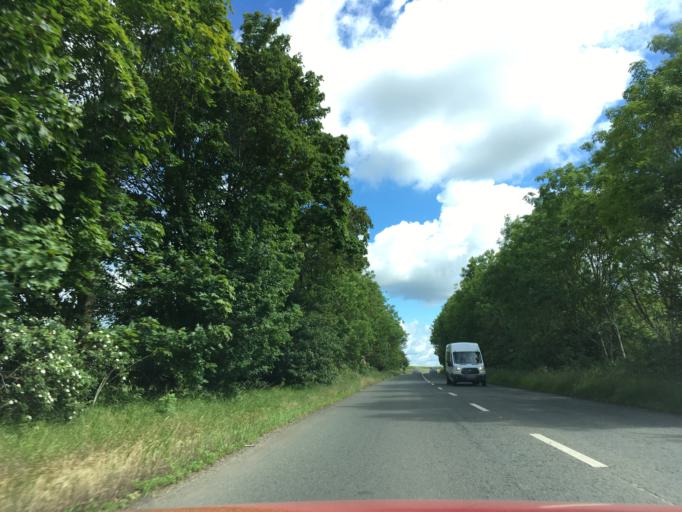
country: GB
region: England
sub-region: Gloucestershire
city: Lechlade
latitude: 51.7367
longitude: -1.6629
